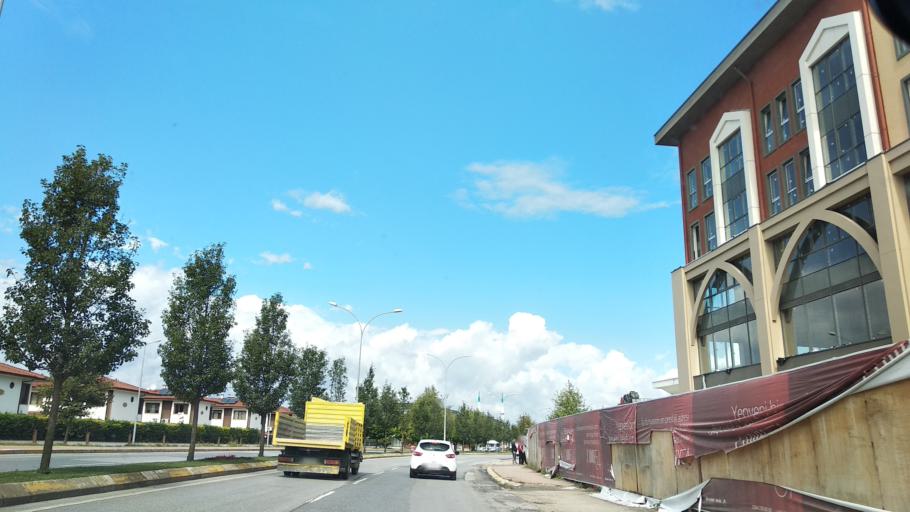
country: TR
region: Sakarya
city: Adapazari
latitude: 40.7754
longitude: 30.3639
